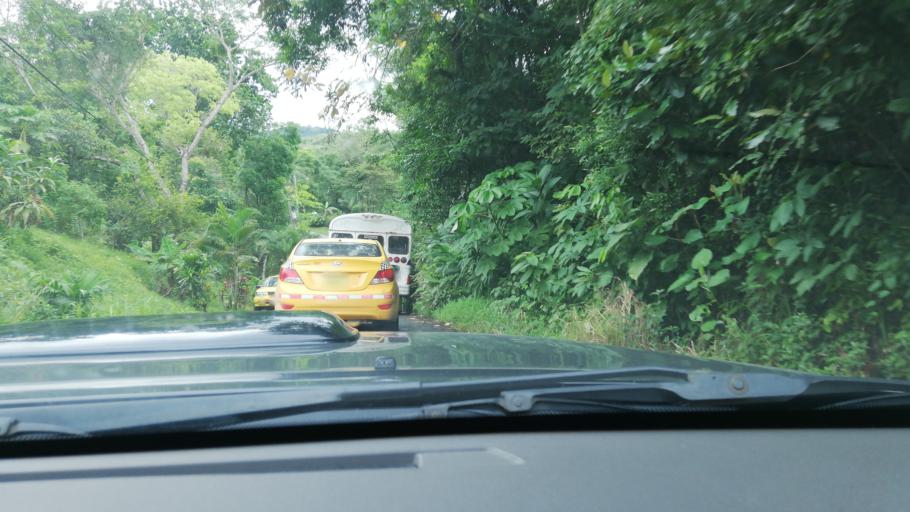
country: PA
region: Panama
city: San Miguelito
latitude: 9.0955
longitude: -79.4491
